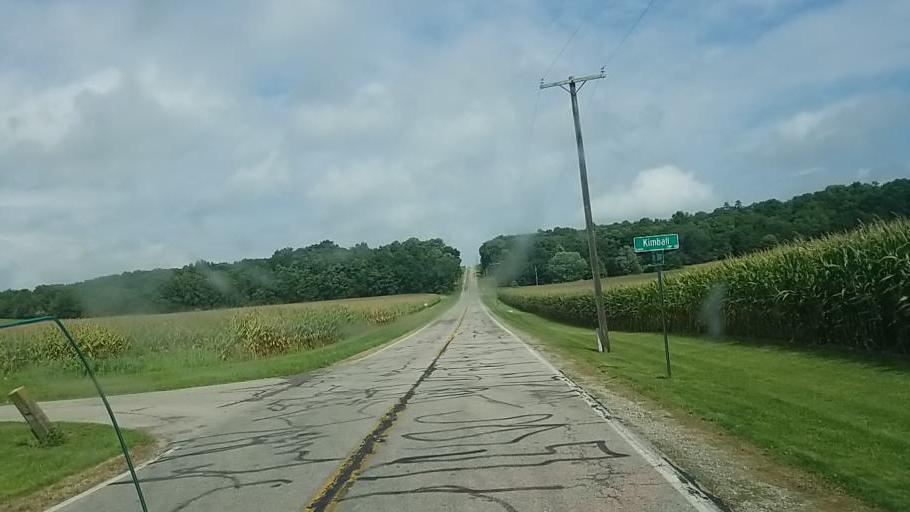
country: US
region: Ohio
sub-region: Logan County
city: West Liberty
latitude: 40.2337
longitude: -83.6847
